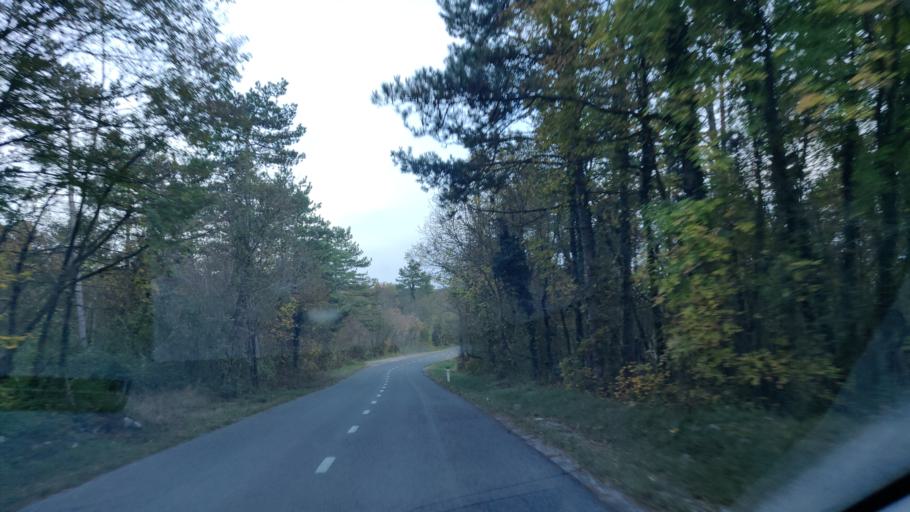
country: IT
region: Friuli Venezia Giulia
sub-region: Provincia di Trieste
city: Zolla
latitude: 45.8024
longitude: 13.8491
